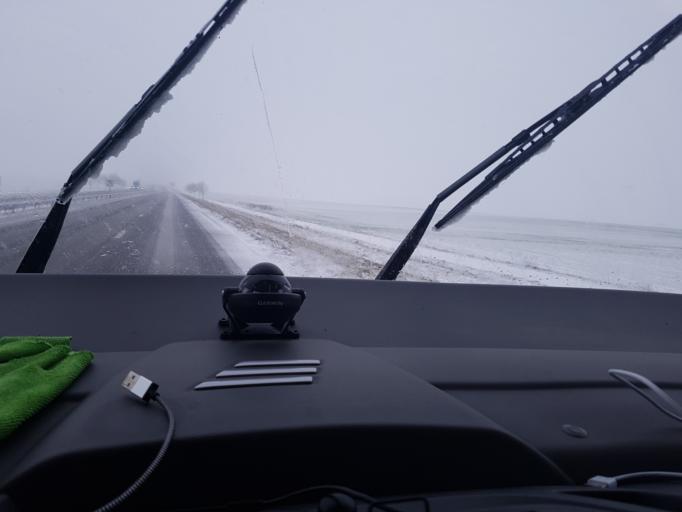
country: FR
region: Lorraine
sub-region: Departement de la Moselle
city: Chateau-Salins
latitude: 48.8570
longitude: 6.4434
